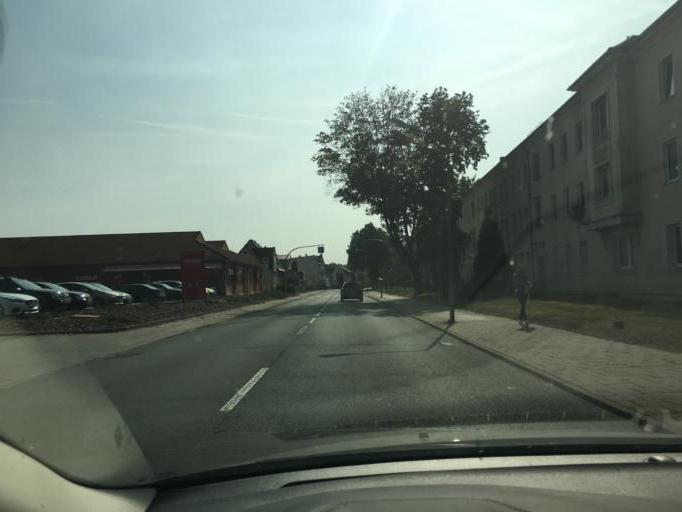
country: DE
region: Saxony-Anhalt
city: Calbe
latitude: 51.9145
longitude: 11.7868
